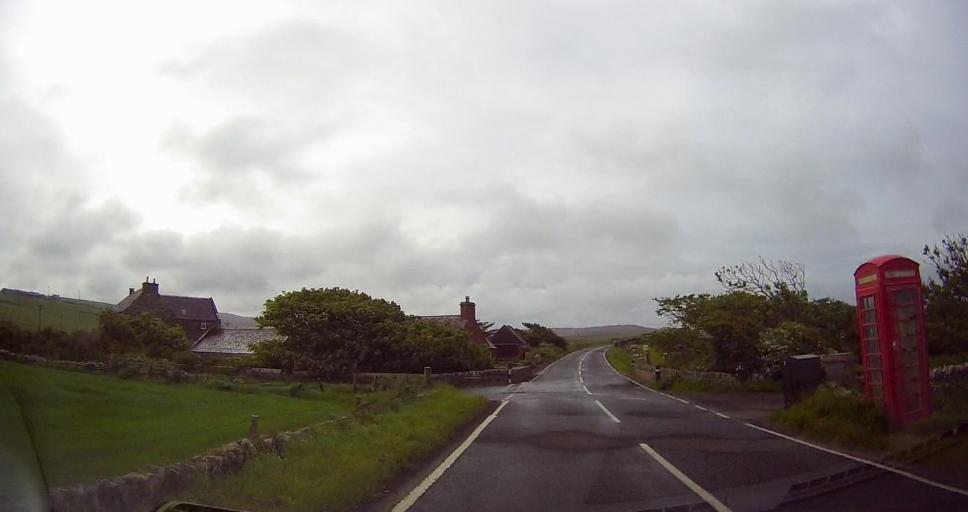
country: GB
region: Scotland
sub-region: Orkney Islands
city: Stromness
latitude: 58.9692
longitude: -3.2297
